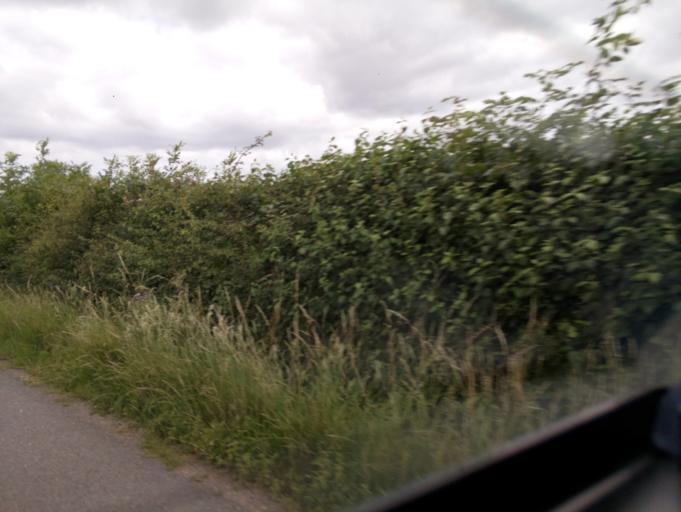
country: GB
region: England
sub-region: Buckinghamshire
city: Newton Longville
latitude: 51.9678
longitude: -0.8171
